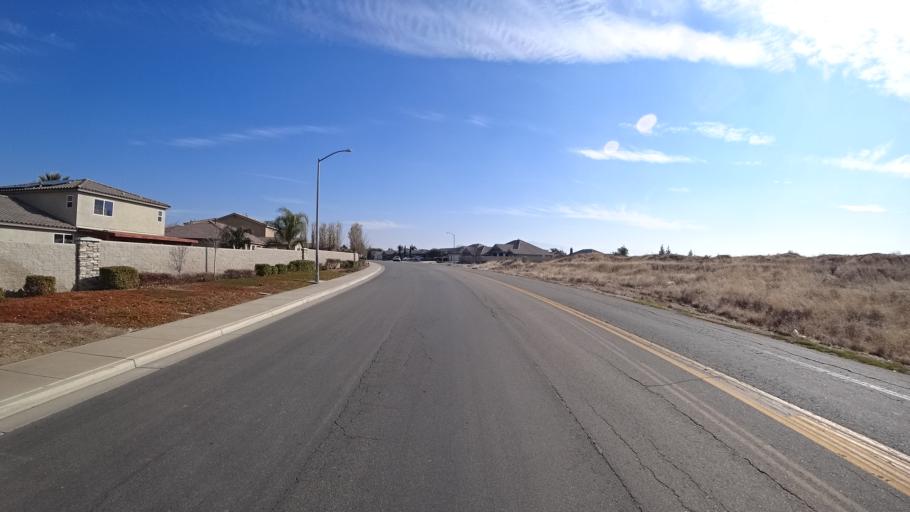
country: US
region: California
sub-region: Kern County
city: Lamont
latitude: 35.3905
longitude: -118.8856
